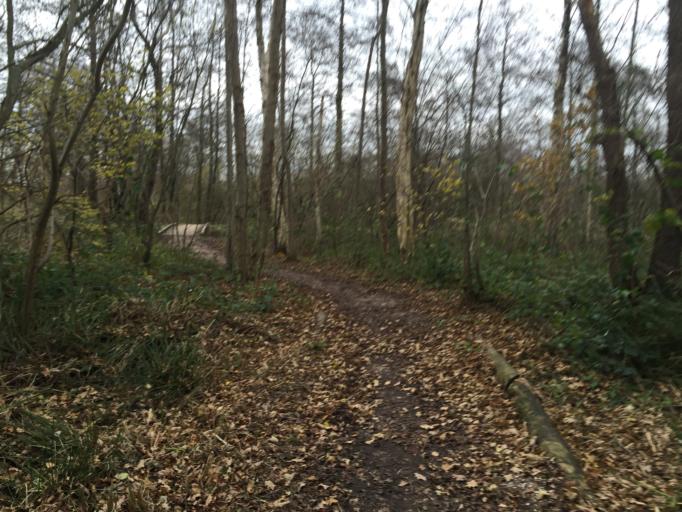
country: NL
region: North Holland
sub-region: Gemeente Weesp
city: Weesp
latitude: 52.2685
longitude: 5.0691
